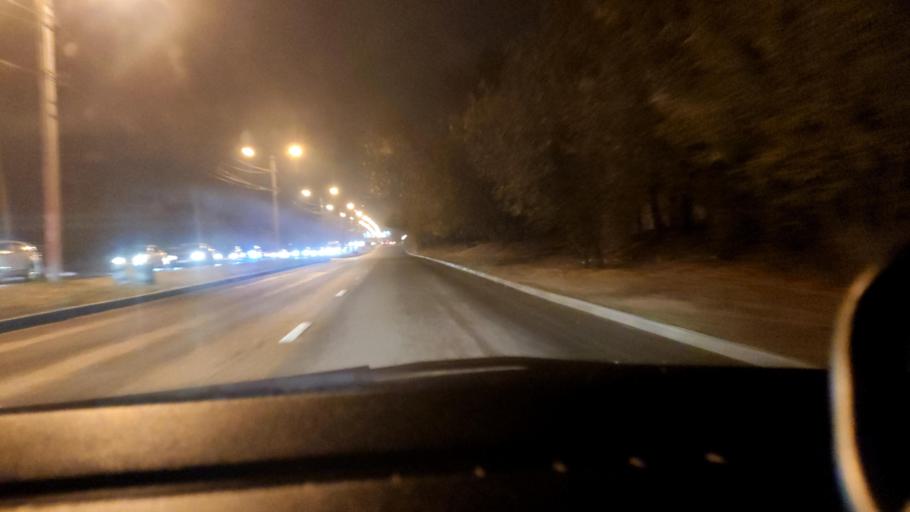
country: RU
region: Voronezj
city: Voronezh
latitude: 51.7085
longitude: 39.1952
